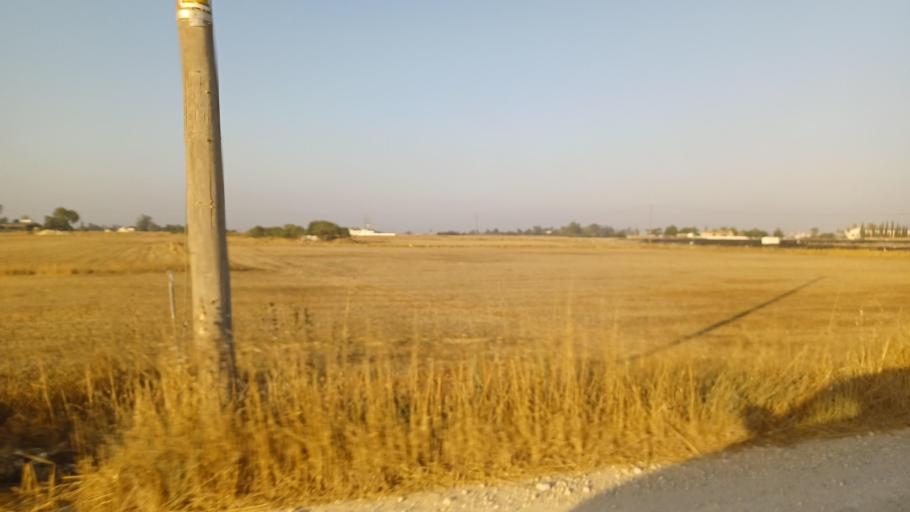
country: CY
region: Ammochostos
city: Avgorou
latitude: 35.0321
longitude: 33.8577
